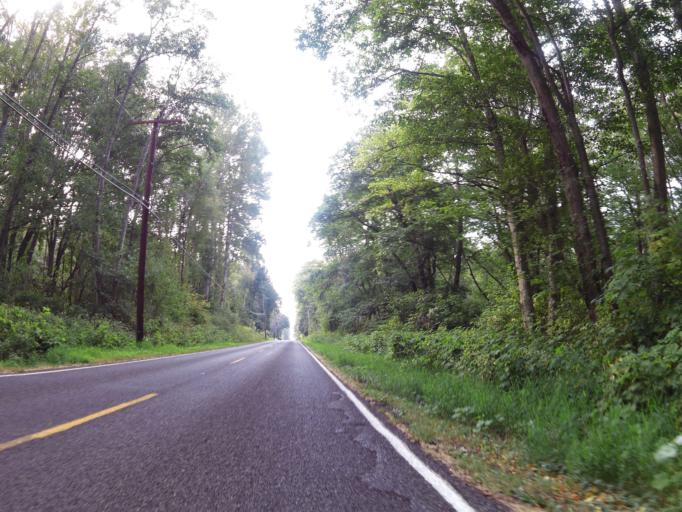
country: US
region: Washington
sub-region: Whatcom County
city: Ferndale
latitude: 48.8172
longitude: -122.6828
